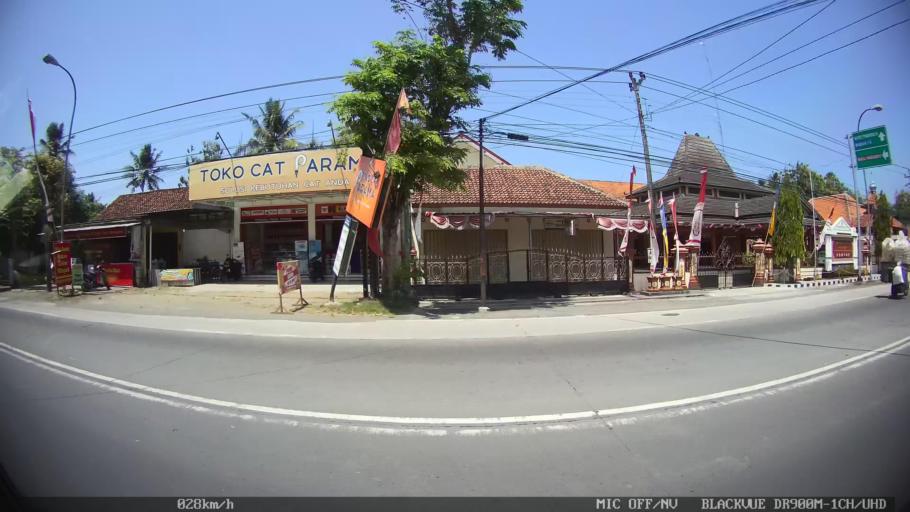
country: ID
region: Daerah Istimewa Yogyakarta
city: Srandakan
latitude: -7.9386
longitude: 110.2471
